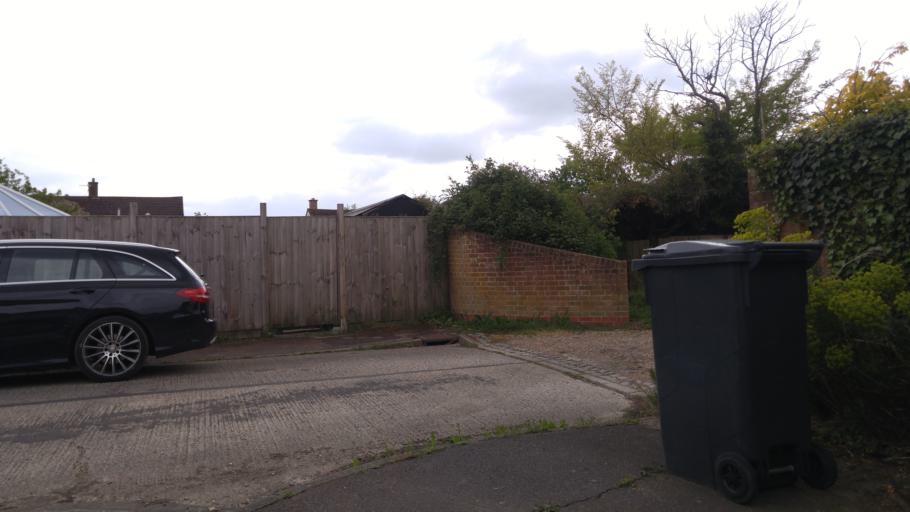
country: GB
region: England
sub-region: Essex
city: Earls Colne
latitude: 51.9430
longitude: 0.6926
